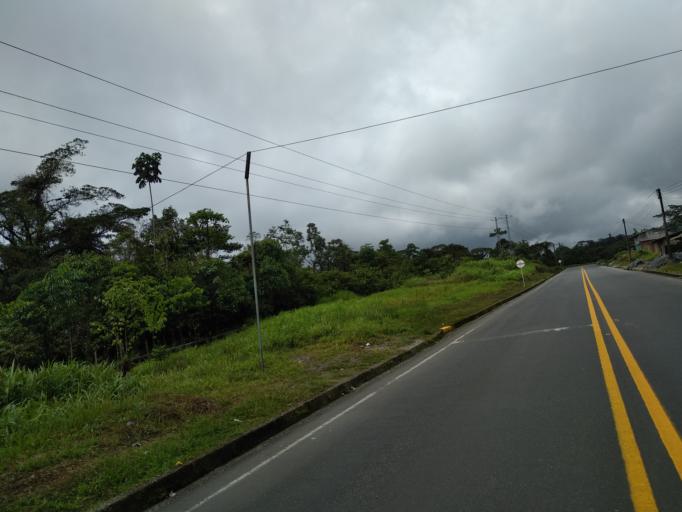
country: CO
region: Narino
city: Ricaurte
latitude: 1.3625
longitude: -78.1794
